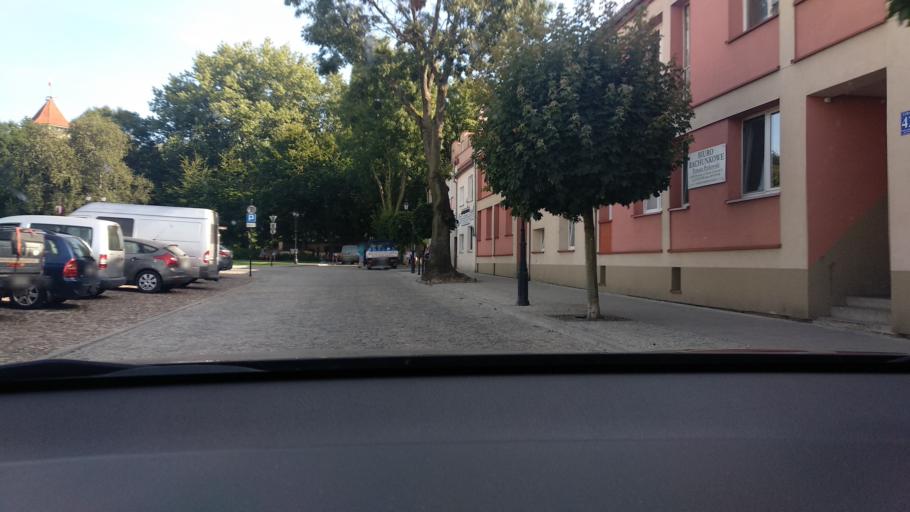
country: PL
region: Masovian Voivodeship
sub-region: Powiat pultuski
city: Pultusk
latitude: 52.7049
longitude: 21.0922
